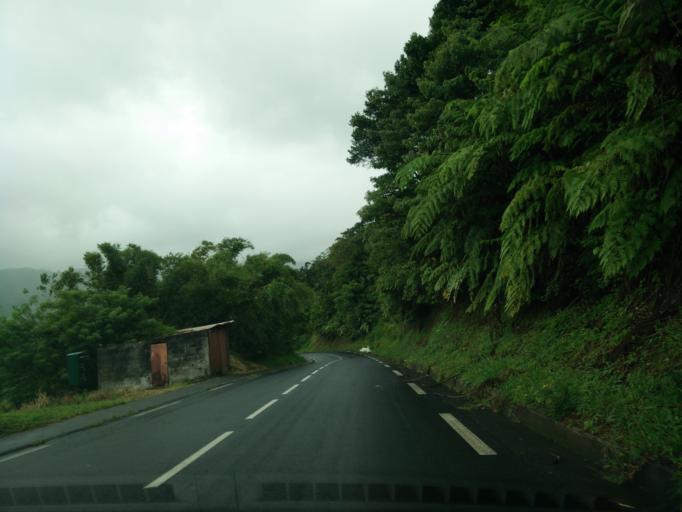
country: MQ
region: Martinique
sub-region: Martinique
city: Le Morne-Rouge
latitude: 14.7713
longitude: -61.1302
